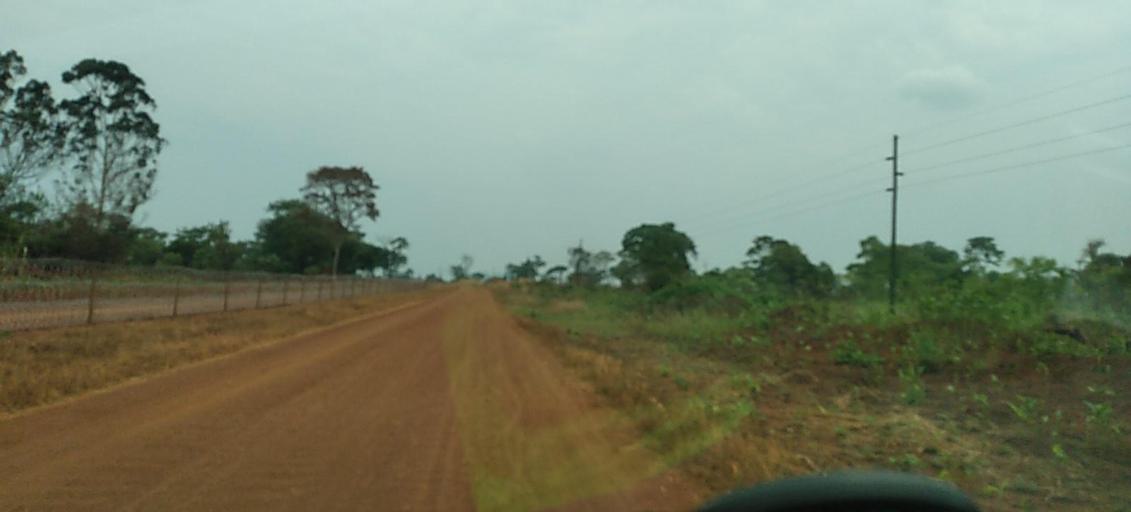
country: ZM
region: North-Western
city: Kansanshi
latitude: -12.0828
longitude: 26.4810
